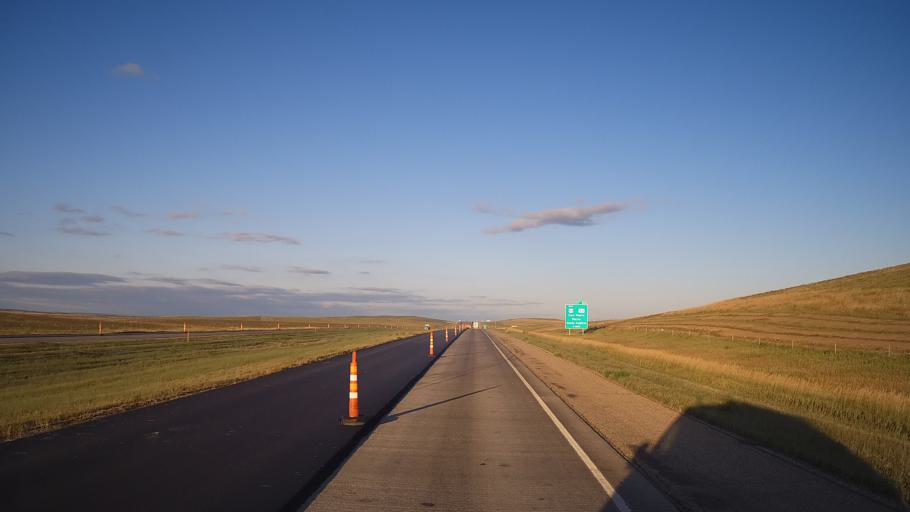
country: US
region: South Dakota
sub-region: Jones County
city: Murdo
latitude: 43.9109
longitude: -100.3629
